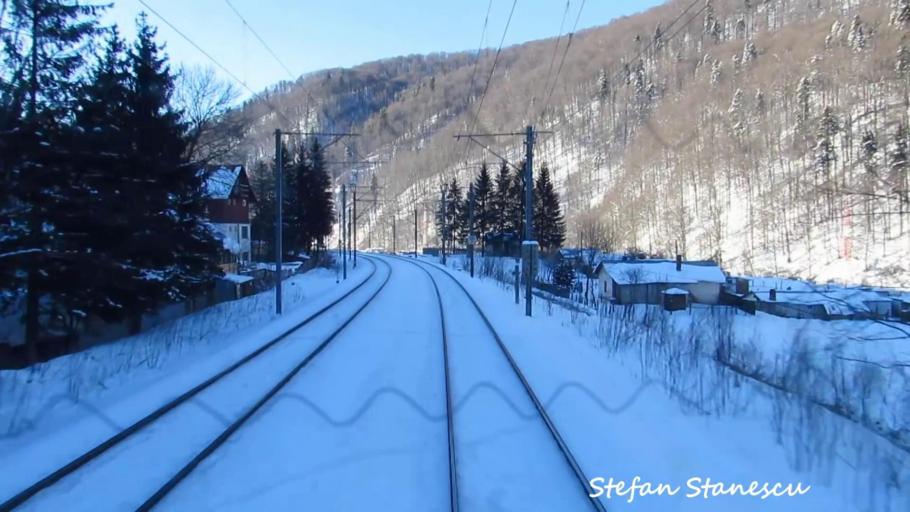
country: RO
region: Prahova
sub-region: Oras Azuga
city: Azuga
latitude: 45.4312
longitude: 25.5530
